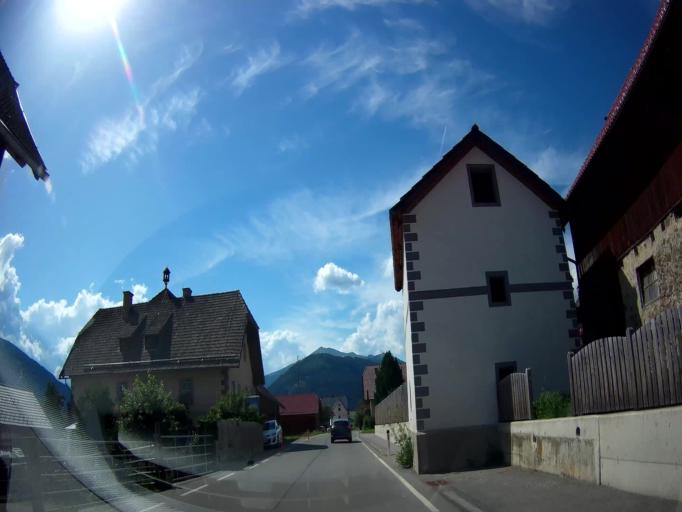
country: AT
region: Salzburg
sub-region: Politischer Bezirk Tamsweg
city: Sankt Margarethen im Lungau
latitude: 47.0862
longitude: 13.7190
